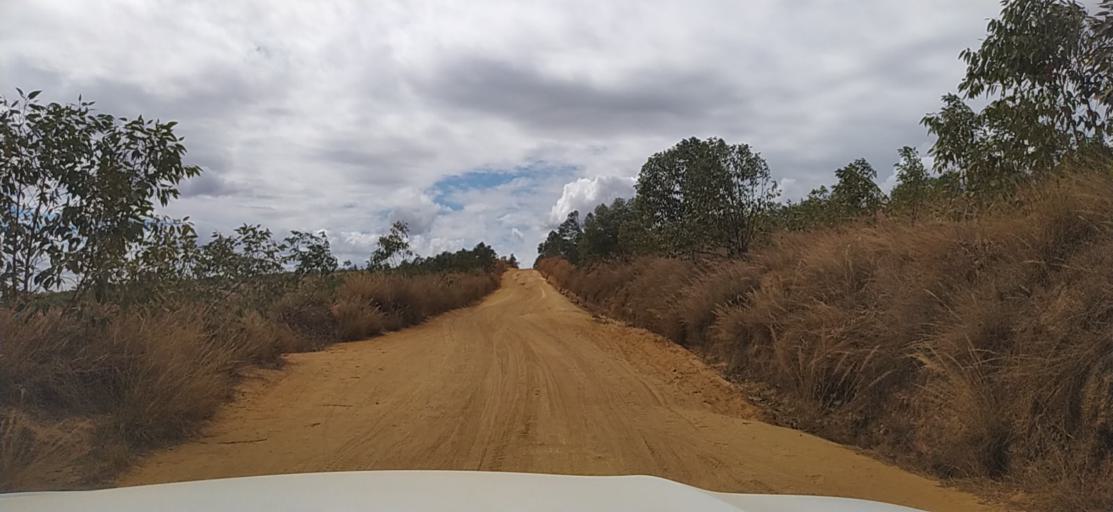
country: MG
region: Alaotra Mangoro
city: Ambatondrazaka
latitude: -17.9498
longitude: 48.2491
